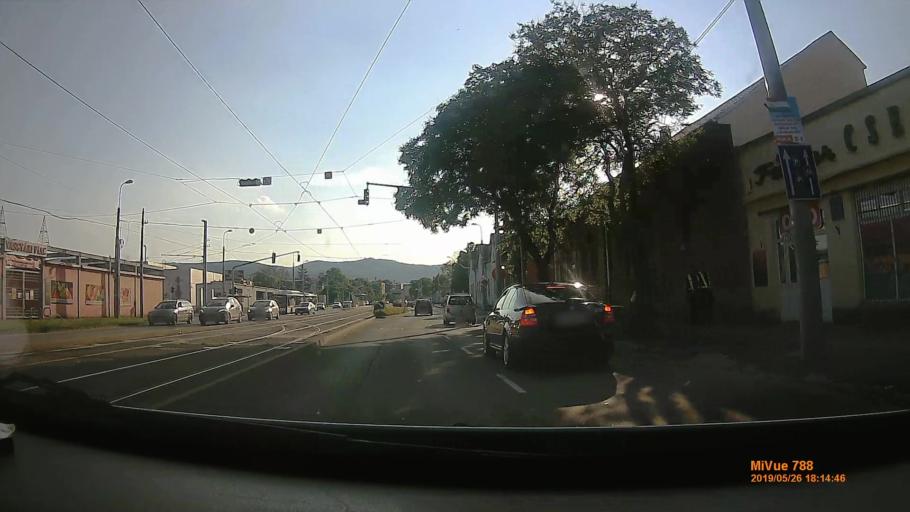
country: HU
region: Borsod-Abauj-Zemplen
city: Miskolc
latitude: 48.1012
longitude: 20.7274
